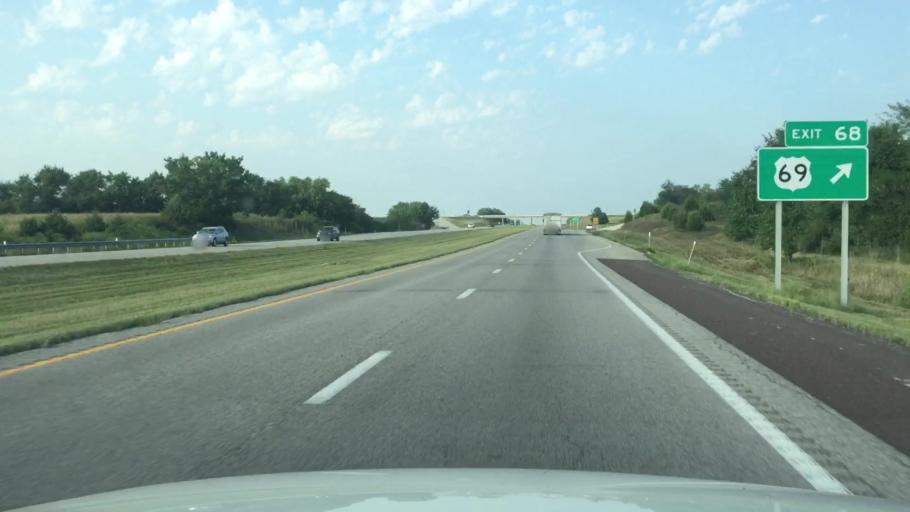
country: US
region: Missouri
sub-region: Daviess County
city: Gallatin
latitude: 39.9405
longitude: -94.1214
